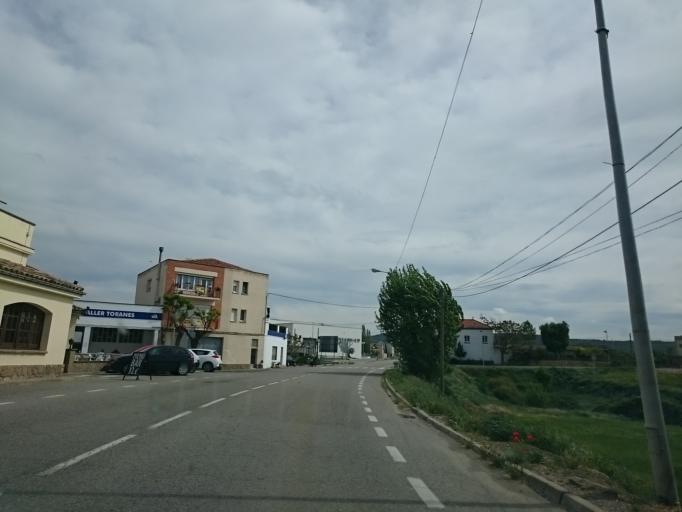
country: ES
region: Catalonia
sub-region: Provincia de Lleida
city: Tora de Riubregos
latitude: 41.8098
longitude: 1.4029
